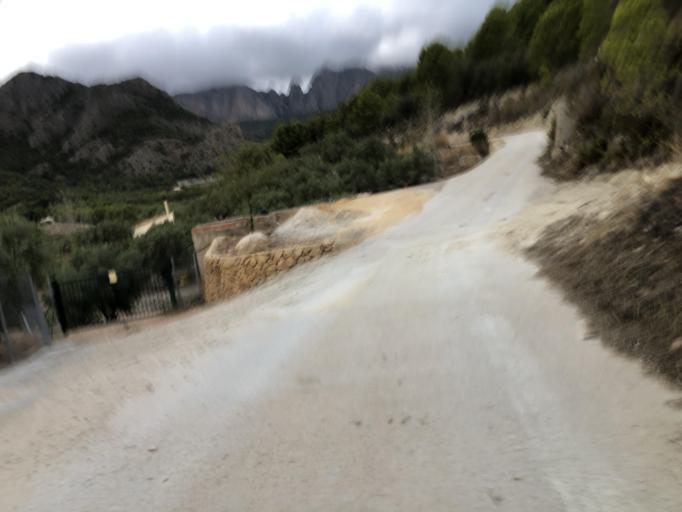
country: ES
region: Valencia
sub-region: Provincia de Alicante
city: Polop
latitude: 38.6353
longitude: -0.1424
